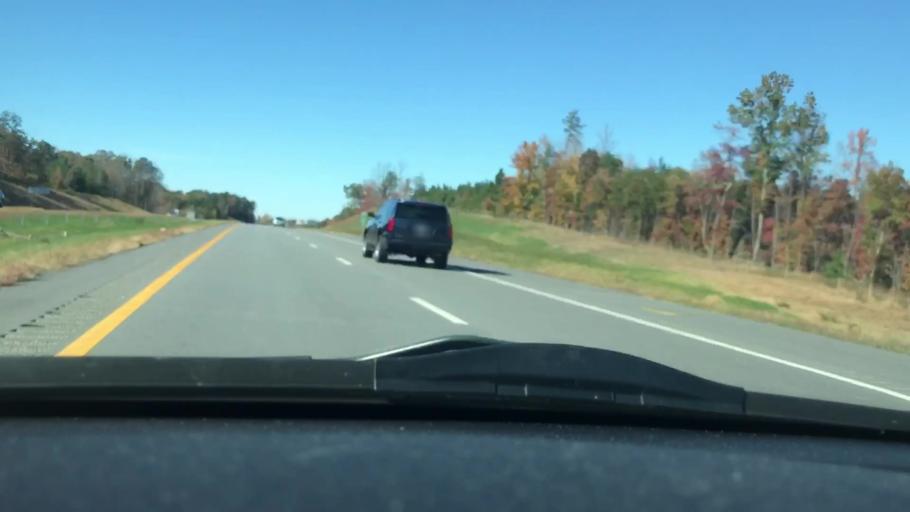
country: US
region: North Carolina
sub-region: Guilford County
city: Stokesdale
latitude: 36.2750
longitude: -79.9345
